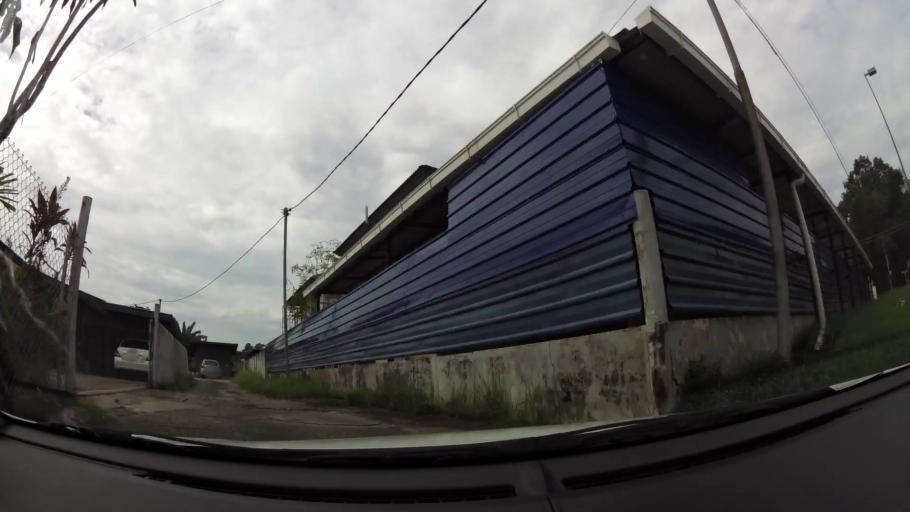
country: BN
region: Brunei and Muara
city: Bandar Seri Begawan
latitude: 4.8843
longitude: 114.8998
